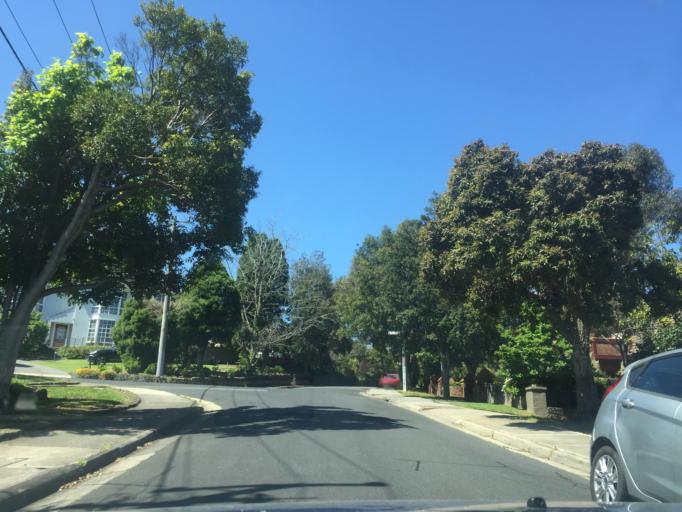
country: AU
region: Victoria
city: Rosanna
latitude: -37.7666
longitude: 145.0605
